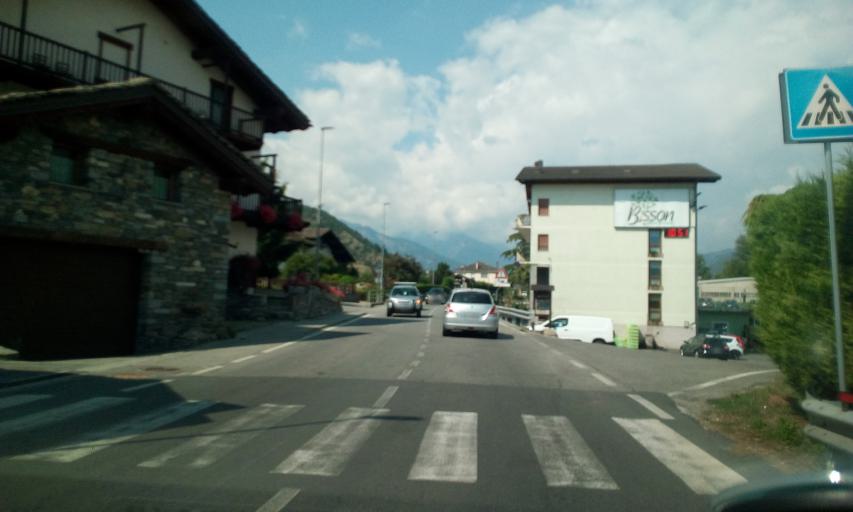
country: IT
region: Aosta Valley
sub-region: Valle d'Aosta
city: Gressan
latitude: 45.7261
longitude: 7.3067
